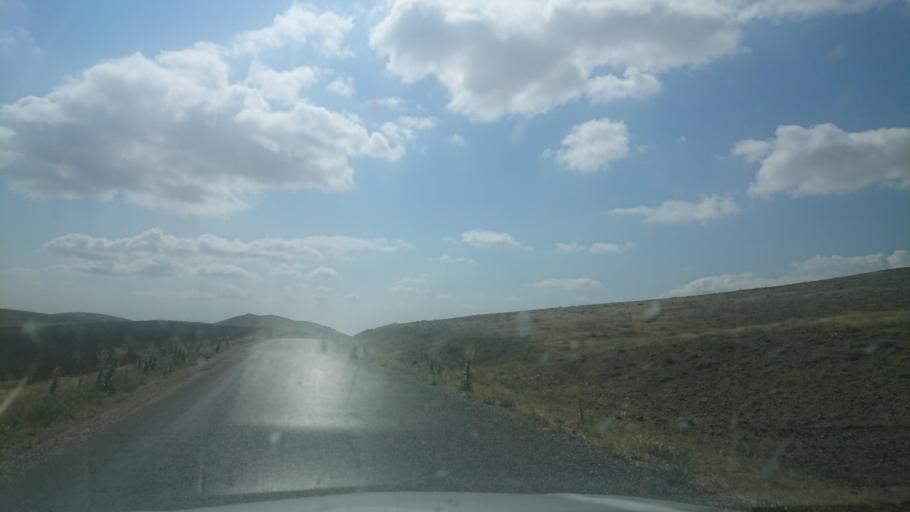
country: TR
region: Aksaray
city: Sariyahsi
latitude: 39.0021
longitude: 33.9712
